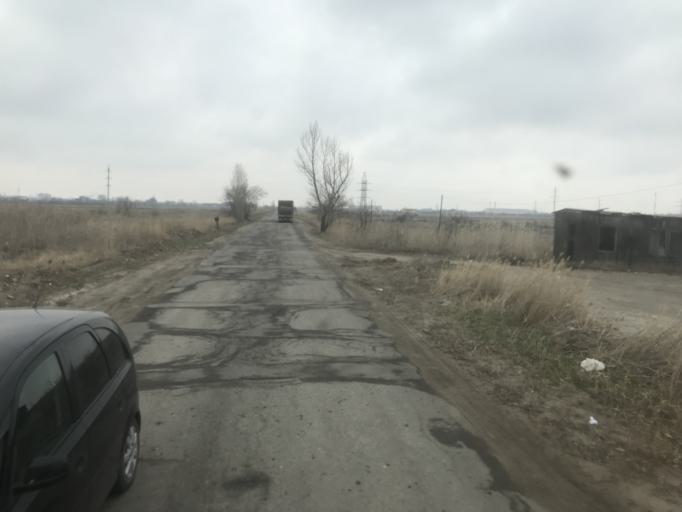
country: RU
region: Volgograd
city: Svetlyy Yar
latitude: 48.5164
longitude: 44.6302
